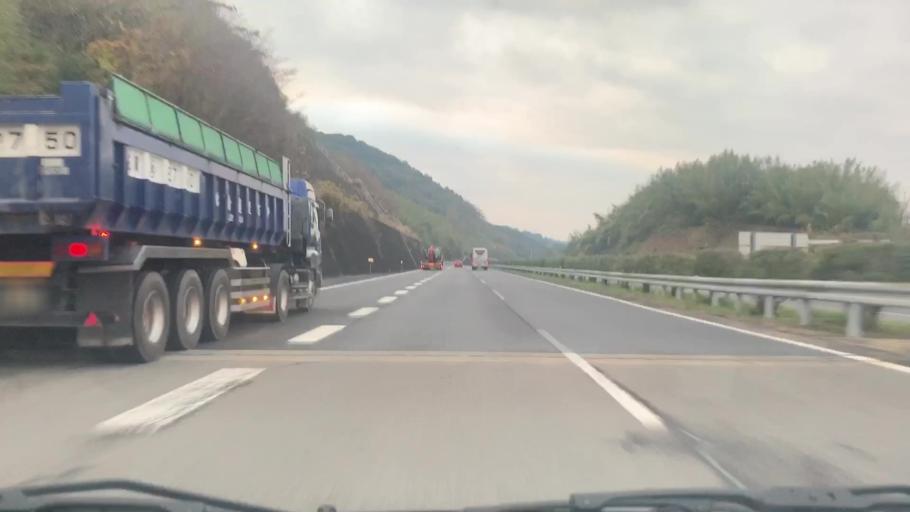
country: JP
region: Nagasaki
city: Omura
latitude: 32.9900
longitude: 129.9567
